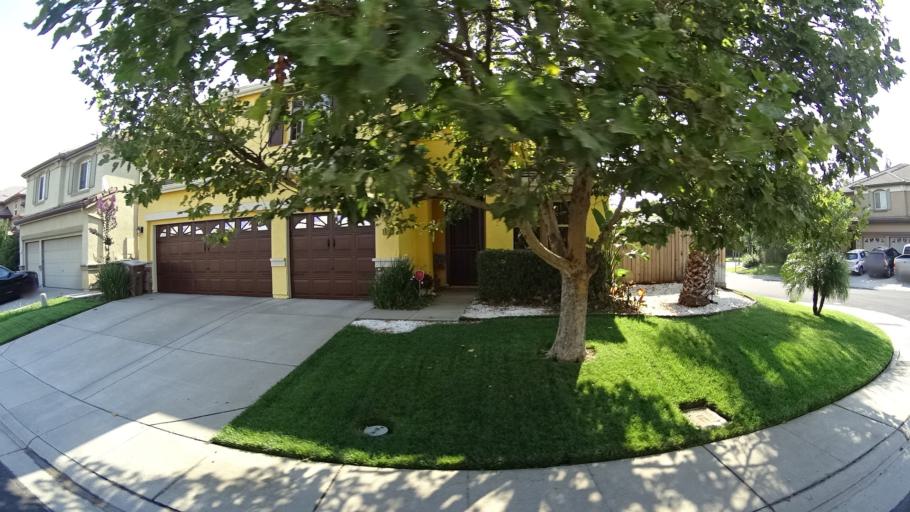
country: US
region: California
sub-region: Sacramento County
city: Laguna
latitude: 38.3871
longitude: -121.4345
